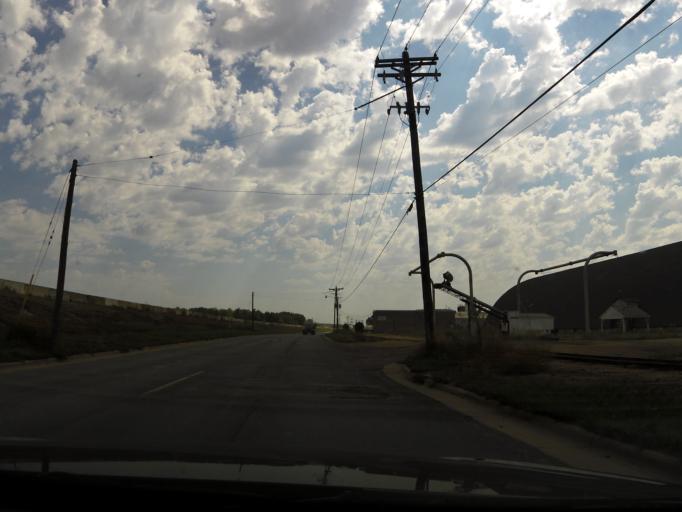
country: US
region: Minnesota
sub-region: Ramsey County
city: Saint Paul
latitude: 44.9396
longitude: -93.0496
